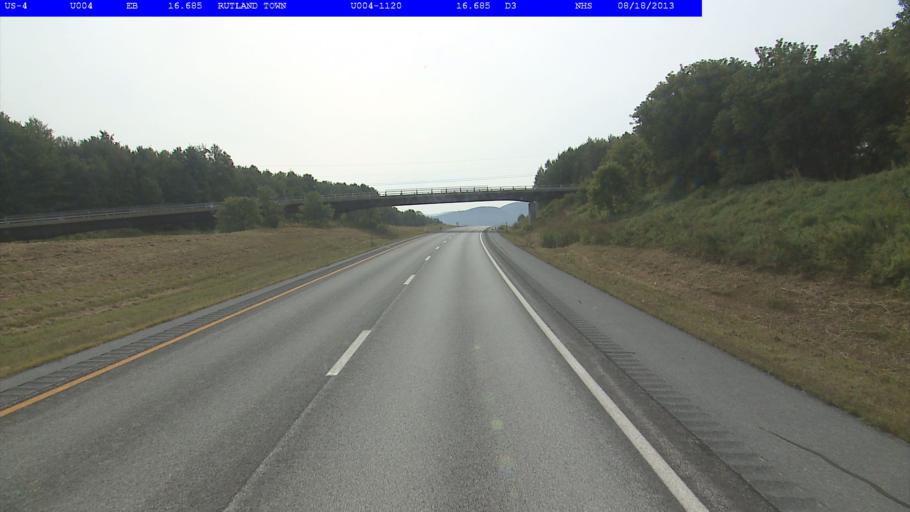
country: US
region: Vermont
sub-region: Rutland County
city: Rutland
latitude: 43.5912
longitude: -73.0055
